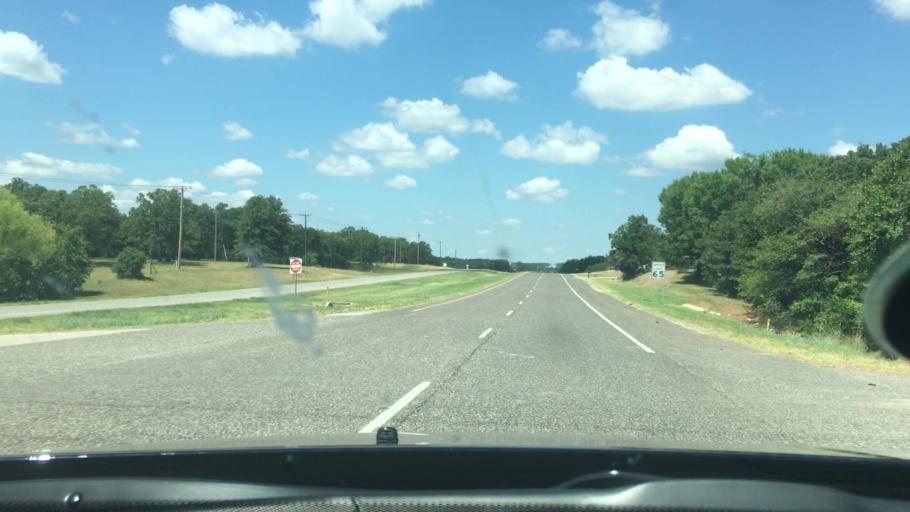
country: US
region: Oklahoma
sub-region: Carter County
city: Lone Grove
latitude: 34.1730
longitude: -97.3347
